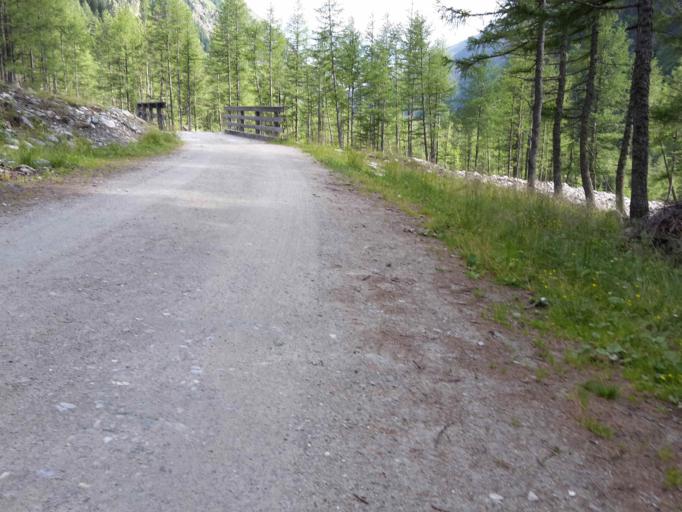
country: AT
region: Tyrol
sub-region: Politischer Bezirk Lienz
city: Matrei in Osttirol
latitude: 47.0678
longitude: 12.6246
